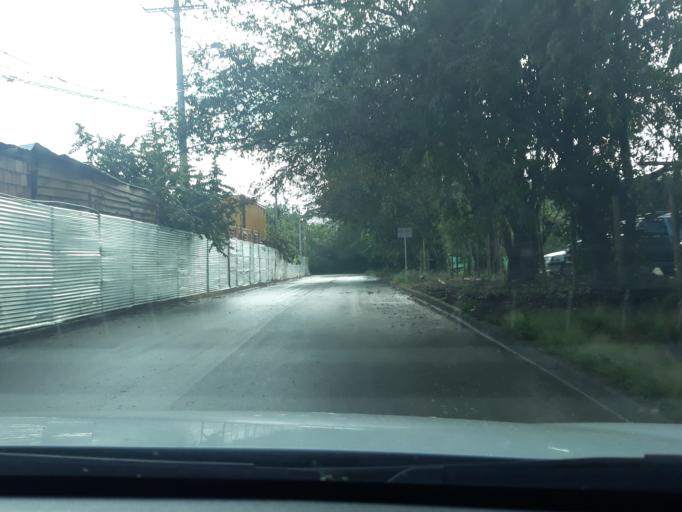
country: CO
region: Valle del Cauca
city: Cali
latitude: 3.3542
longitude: -76.5174
